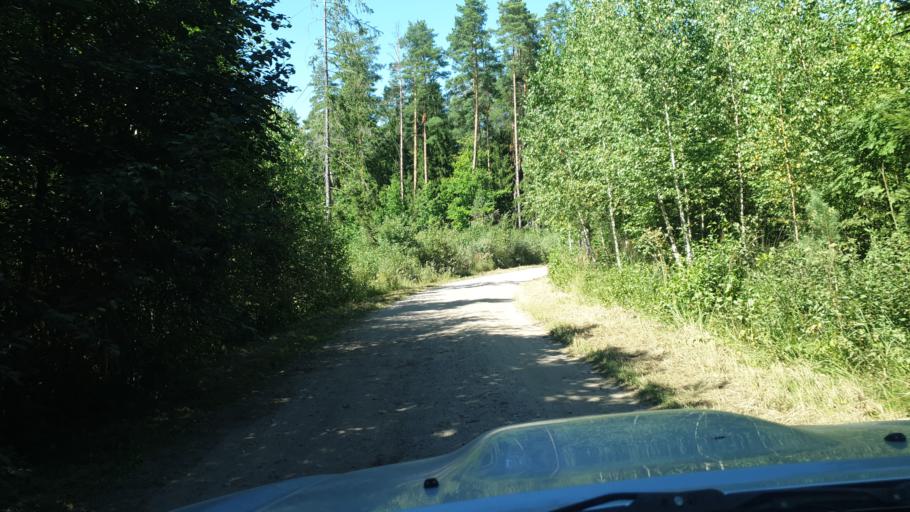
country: LT
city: Sirvintos
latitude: 54.9125
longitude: 24.9276
